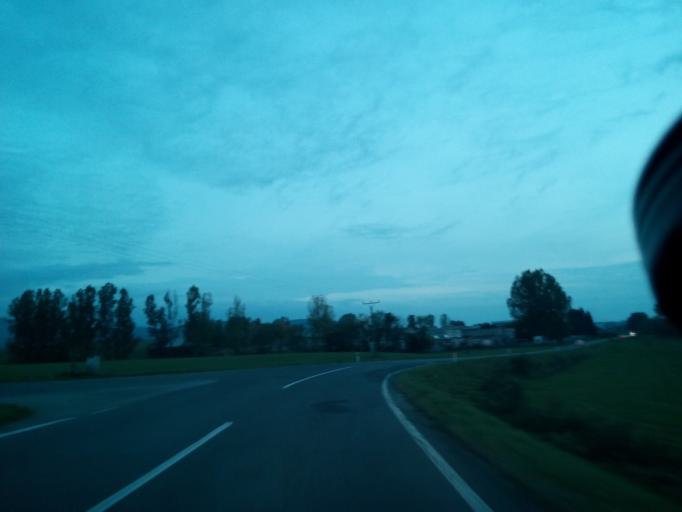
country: SK
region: Presovsky
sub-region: Okres Presov
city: Presov
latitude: 49.0591
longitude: 21.3451
